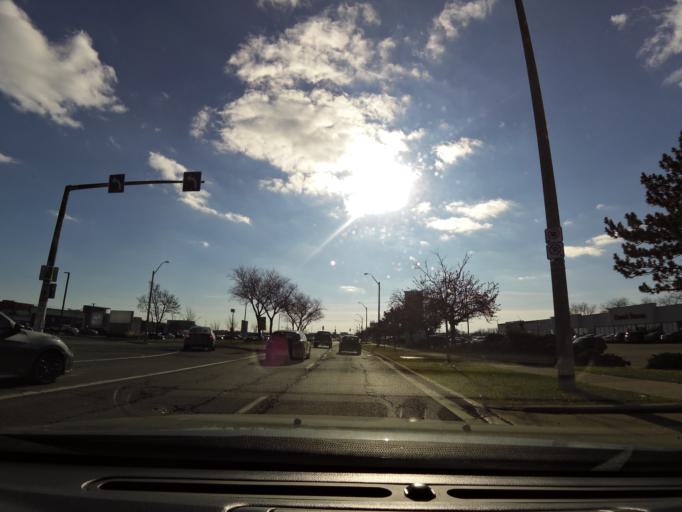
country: CA
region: Ontario
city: Hamilton
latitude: 43.2200
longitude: -79.8635
